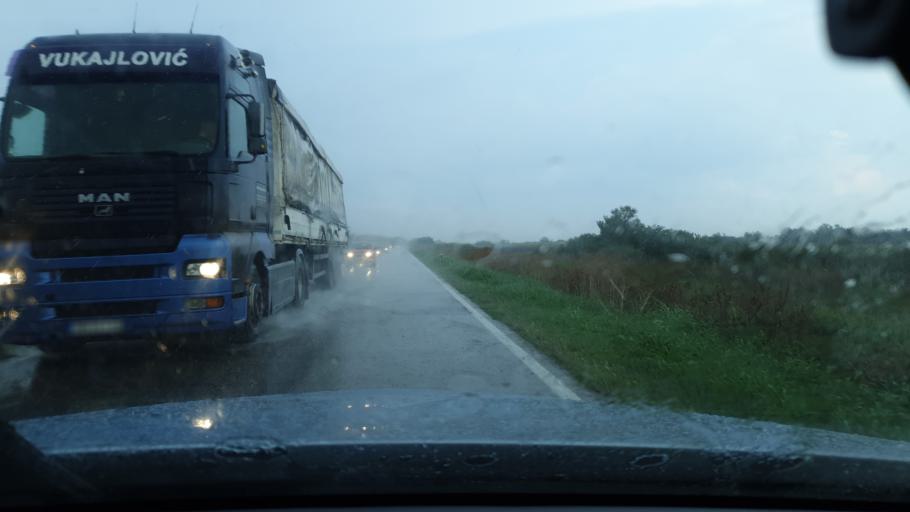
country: RS
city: Banatski Despotovac
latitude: 45.3874
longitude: 20.6180
